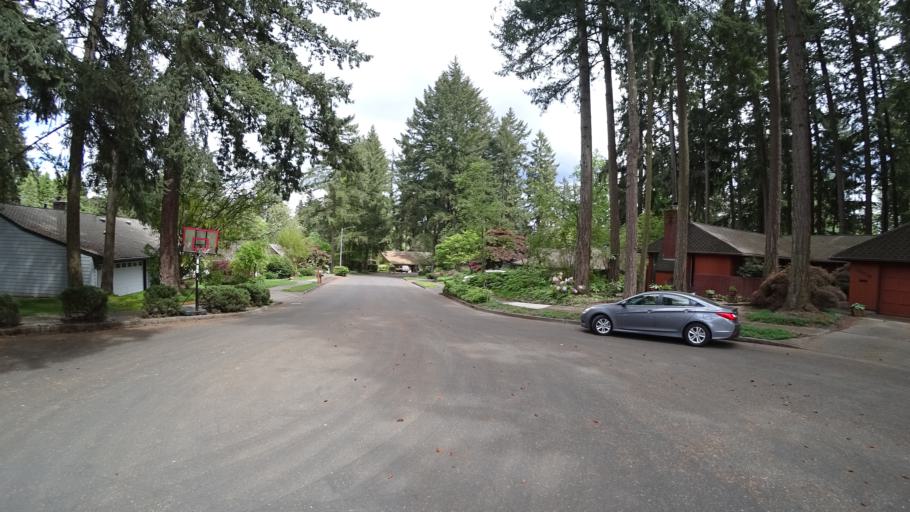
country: US
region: Oregon
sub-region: Washington County
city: Beaverton
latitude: 45.4792
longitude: -122.8357
